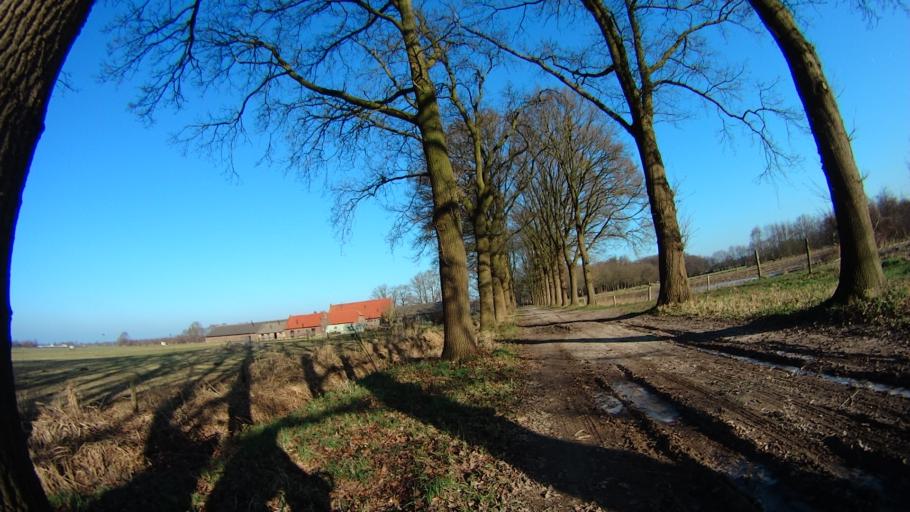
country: NL
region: Utrecht
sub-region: Gemeente Amersfoort
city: Hoogland
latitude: 52.1785
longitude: 5.3452
